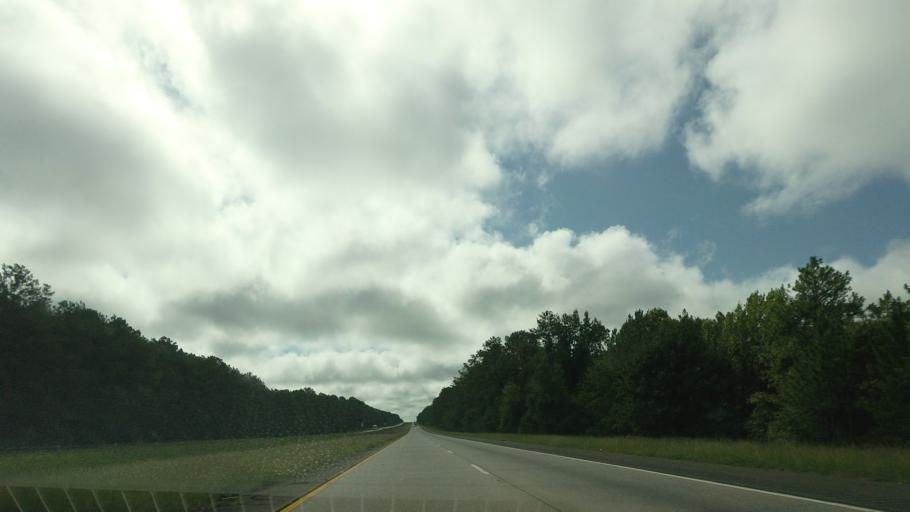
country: US
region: Georgia
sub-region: Houston County
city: Warner Robins
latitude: 32.7121
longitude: -83.5220
